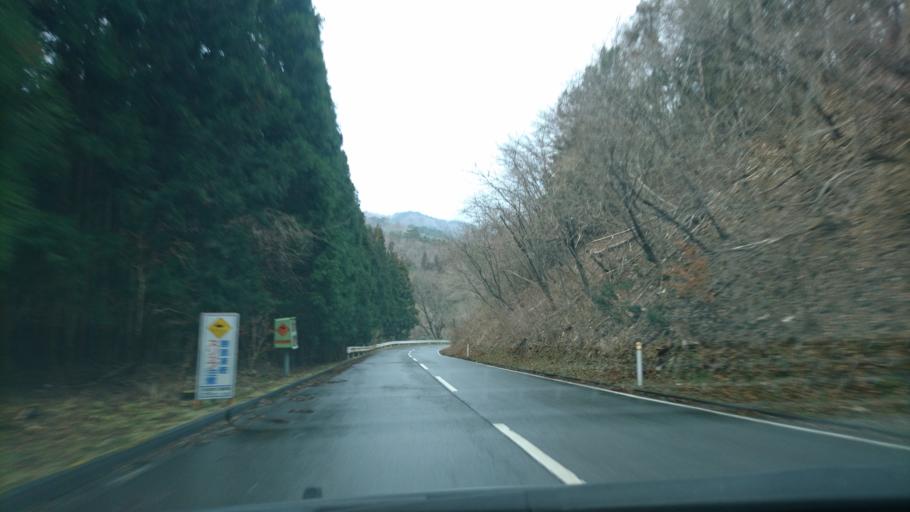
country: JP
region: Iwate
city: Ofunato
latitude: 38.9983
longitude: 141.5489
